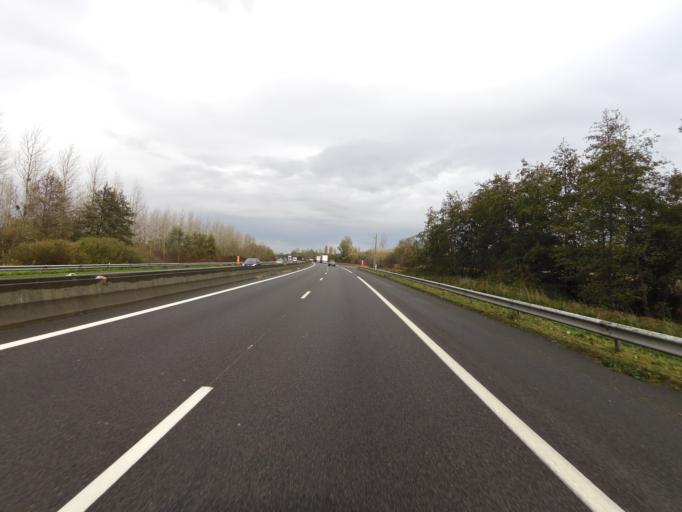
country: FR
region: Rhone-Alpes
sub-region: Departement du Rhone
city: Marennes
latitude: 45.6231
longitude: 4.8937
